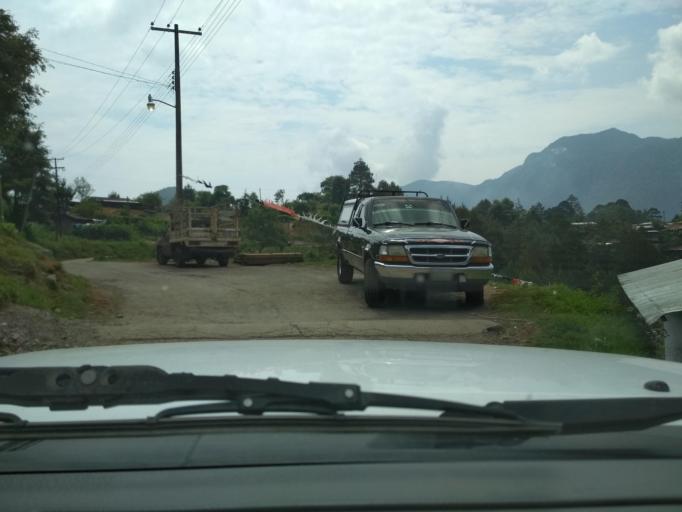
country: MX
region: Veracruz
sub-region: Camerino Z. Mendoza
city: Necoxtla
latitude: 18.7761
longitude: -97.1517
